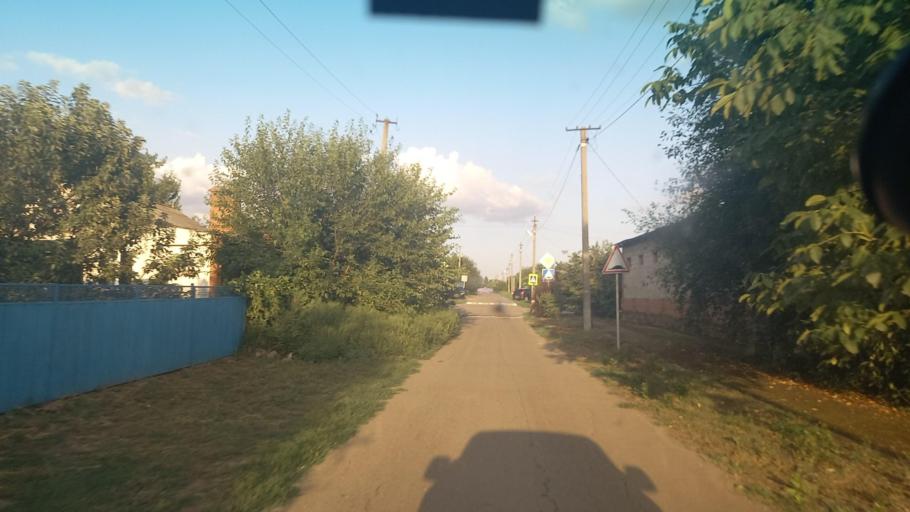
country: RU
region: Adygeya
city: Khatukay
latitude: 45.2944
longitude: 39.5536
